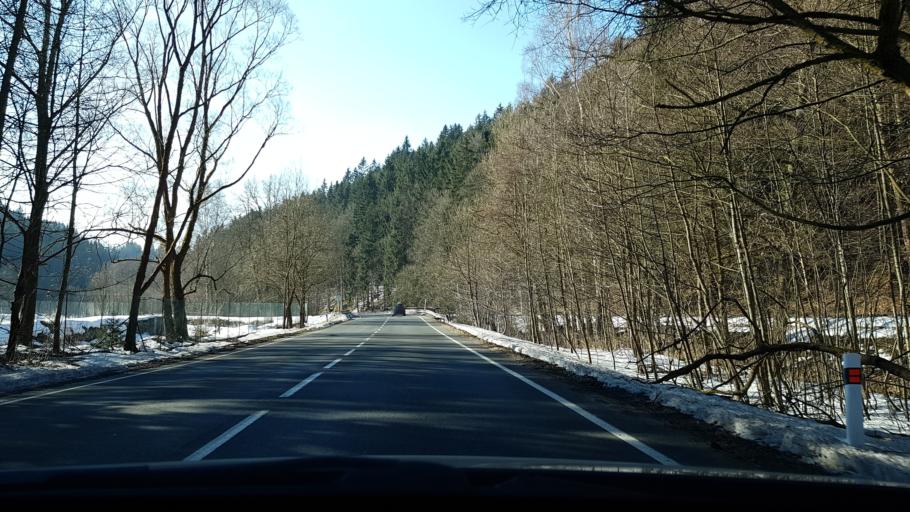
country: CZ
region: Olomoucky
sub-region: Okres Sumperk
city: Stare Mesto
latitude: 50.1329
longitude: 17.0120
